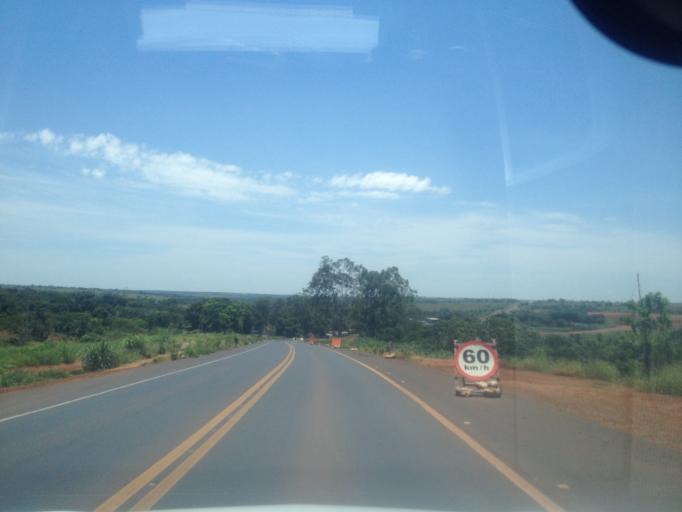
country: BR
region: Minas Gerais
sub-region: Monte Alegre De Minas
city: Monte Alegre de Minas
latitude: -18.8788
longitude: -49.0659
